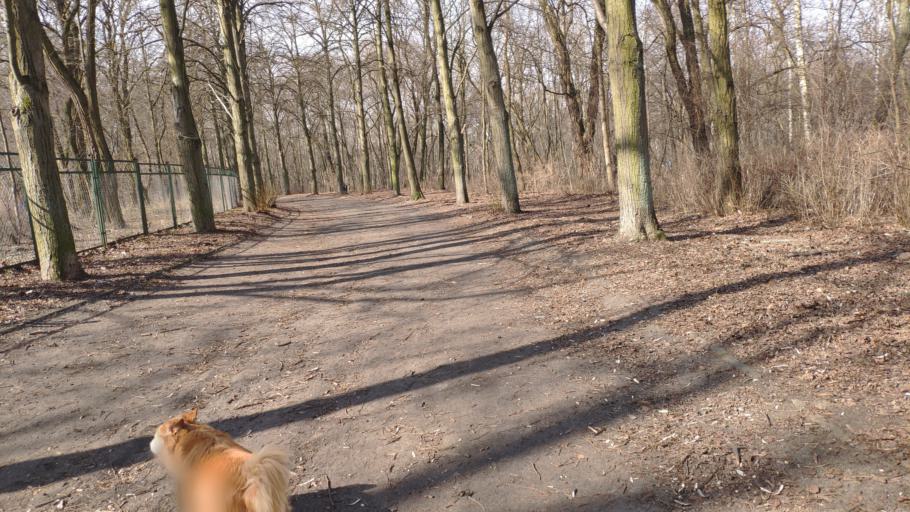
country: PL
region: Lodz Voivodeship
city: Lodz
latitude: 51.7732
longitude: 19.4107
